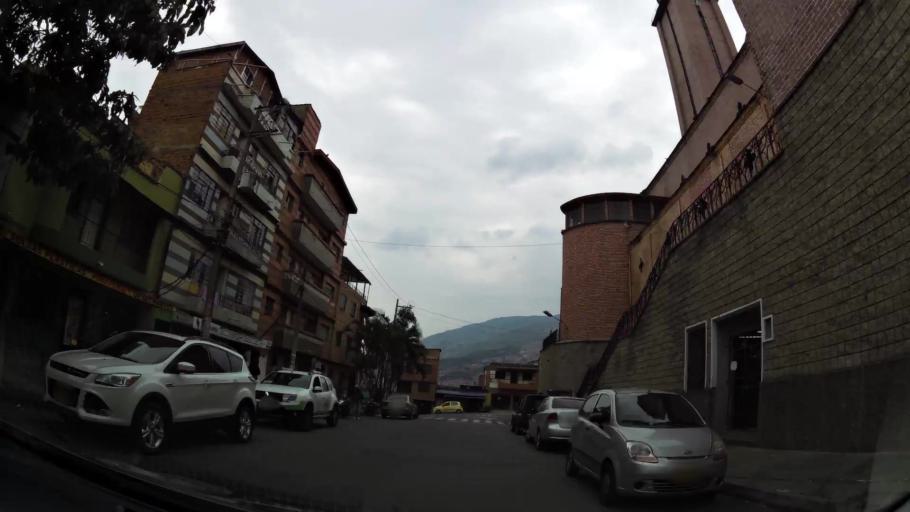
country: CO
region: Antioquia
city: Medellin
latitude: 6.2358
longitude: -75.5542
